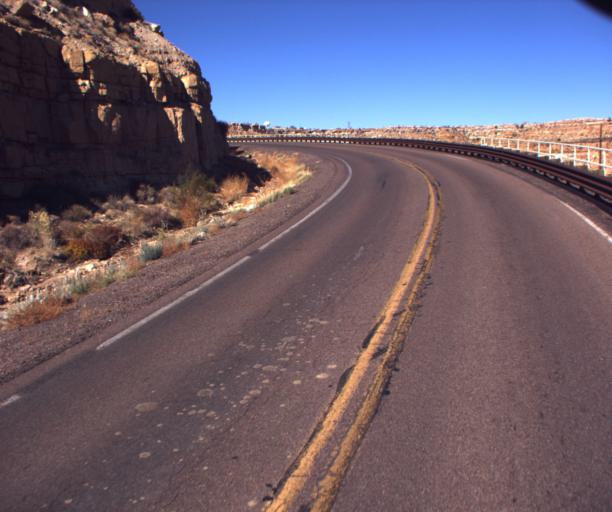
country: US
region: Arizona
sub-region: Navajo County
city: First Mesa
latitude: 35.8086
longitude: -110.5220
